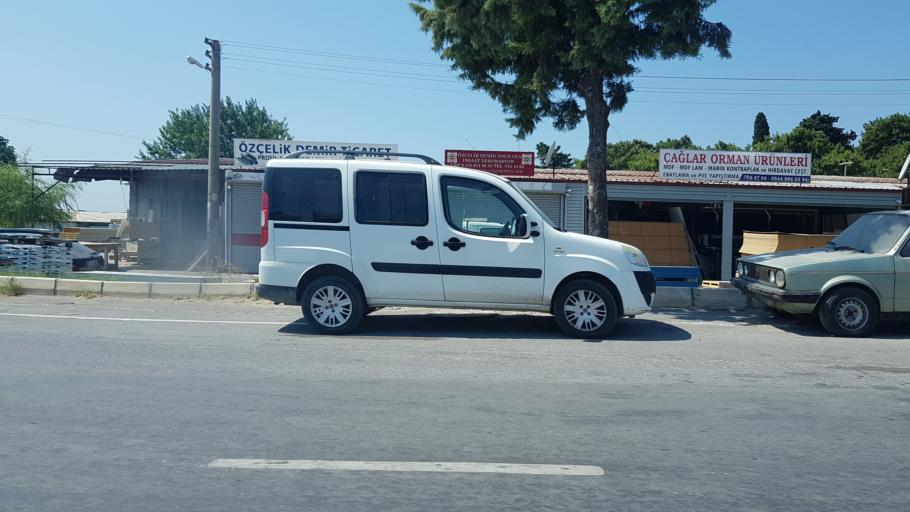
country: TR
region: Izmir
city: Urla
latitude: 38.3215
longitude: 26.7528
